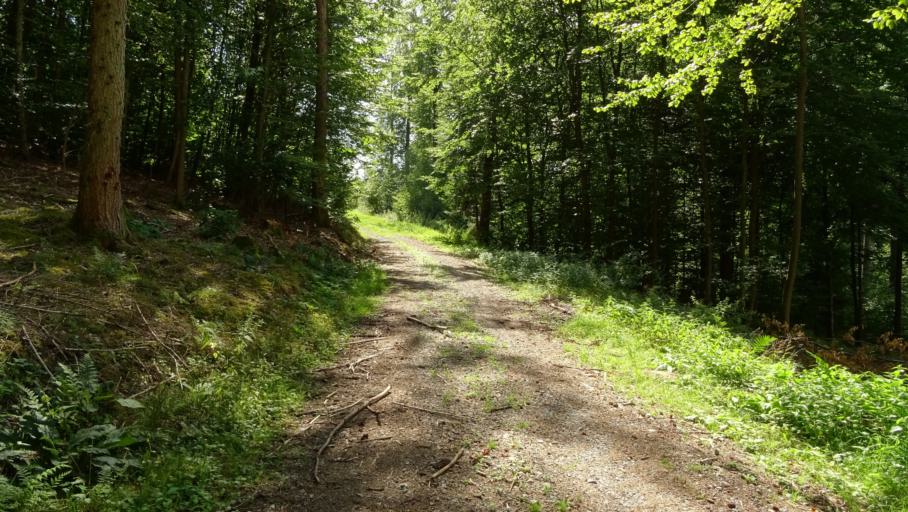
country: DE
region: Baden-Wuerttemberg
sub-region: Karlsruhe Region
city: Neckargerach
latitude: 49.4146
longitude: 9.1084
